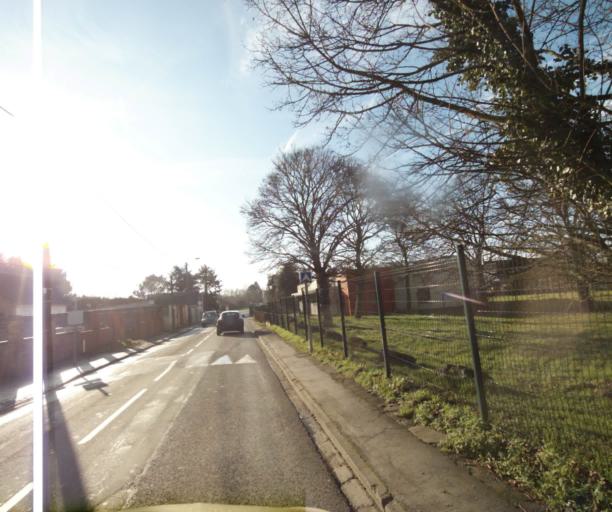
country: FR
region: Nord-Pas-de-Calais
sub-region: Departement du Nord
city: Marly
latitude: 50.3387
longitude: 3.5603
